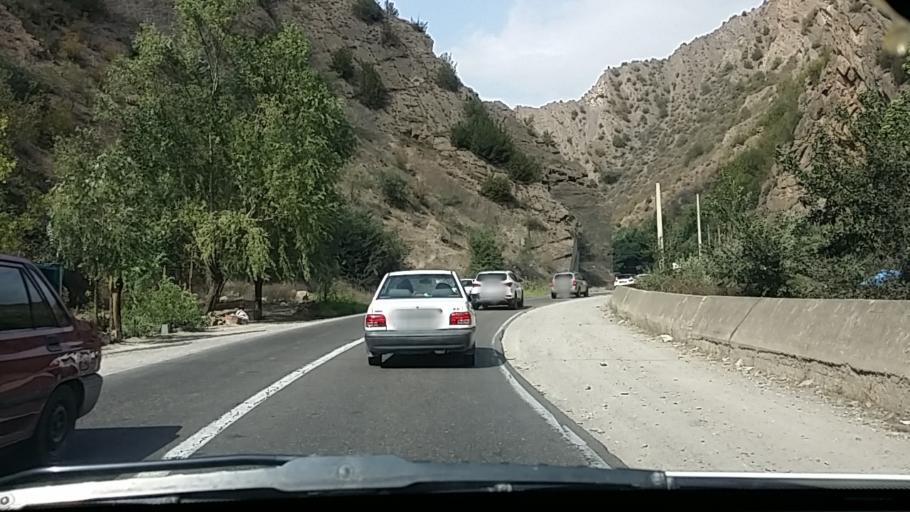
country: IR
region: Mazandaran
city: Chalus
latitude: 36.3105
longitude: 51.2477
